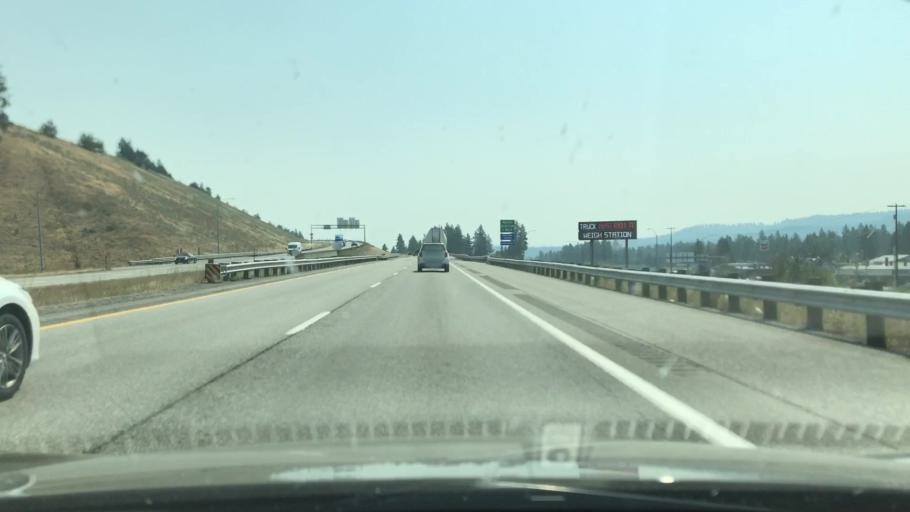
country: US
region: Idaho
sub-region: Kootenai County
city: Post Falls
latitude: 47.7108
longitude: -116.8968
